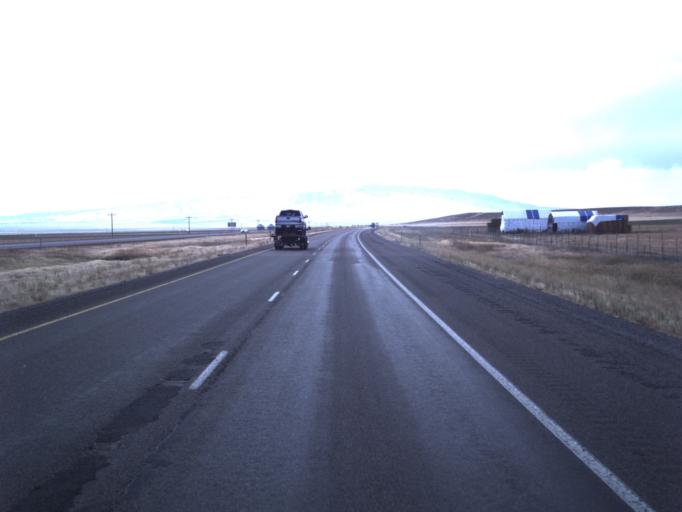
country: US
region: Idaho
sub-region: Oneida County
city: Malad City
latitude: 41.9764
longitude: -112.7912
